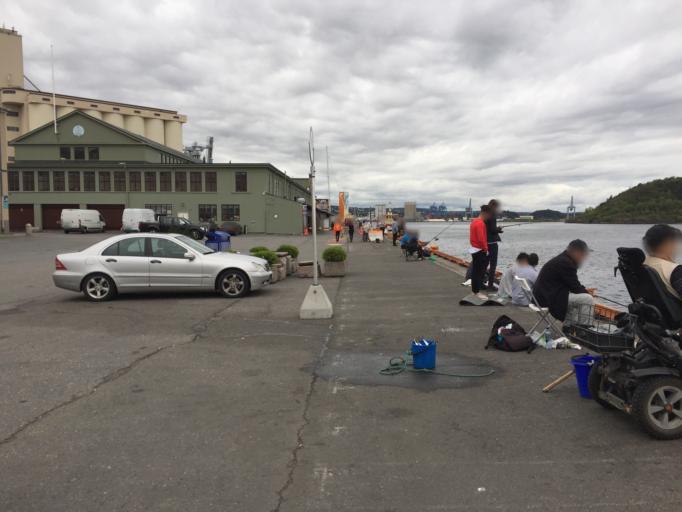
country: NO
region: Oslo
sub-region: Oslo
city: Oslo
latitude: 59.9034
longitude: 10.7387
